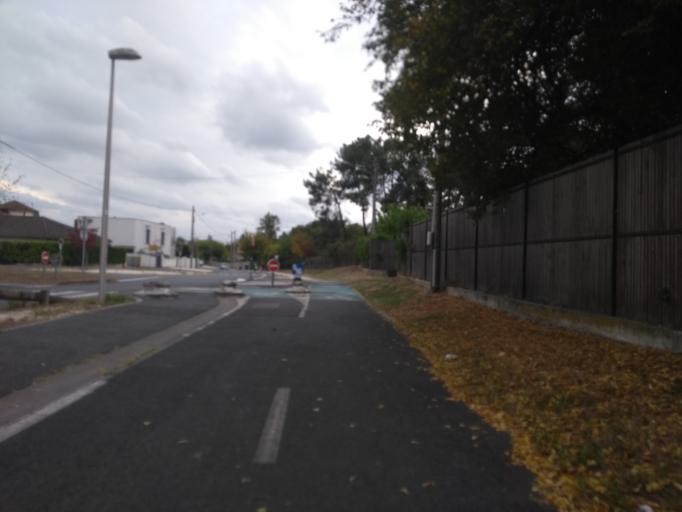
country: FR
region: Aquitaine
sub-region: Departement de la Gironde
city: Talence
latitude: 44.7832
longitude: -0.5935
